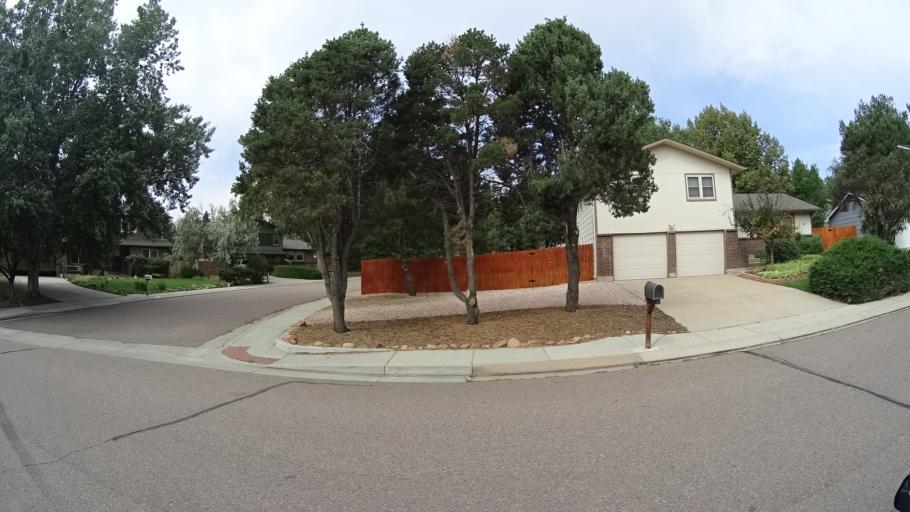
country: US
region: Colorado
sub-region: El Paso County
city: Air Force Academy
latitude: 38.9268
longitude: -104.8346
